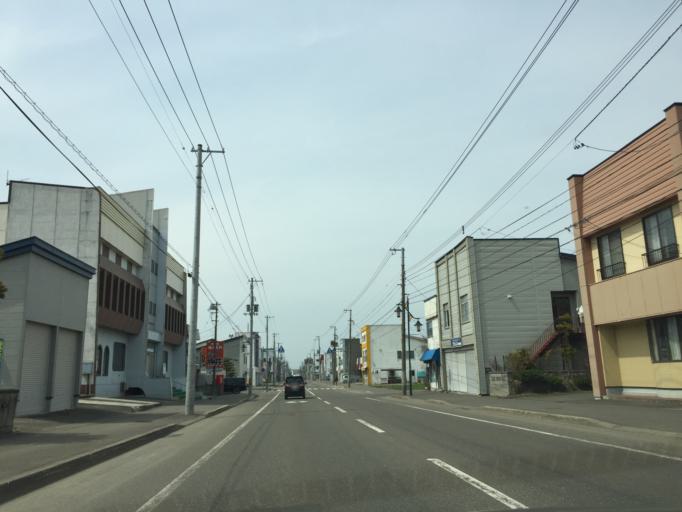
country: JP
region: Hokkaido
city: Akabira
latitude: 43.5523
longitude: 142.0549
